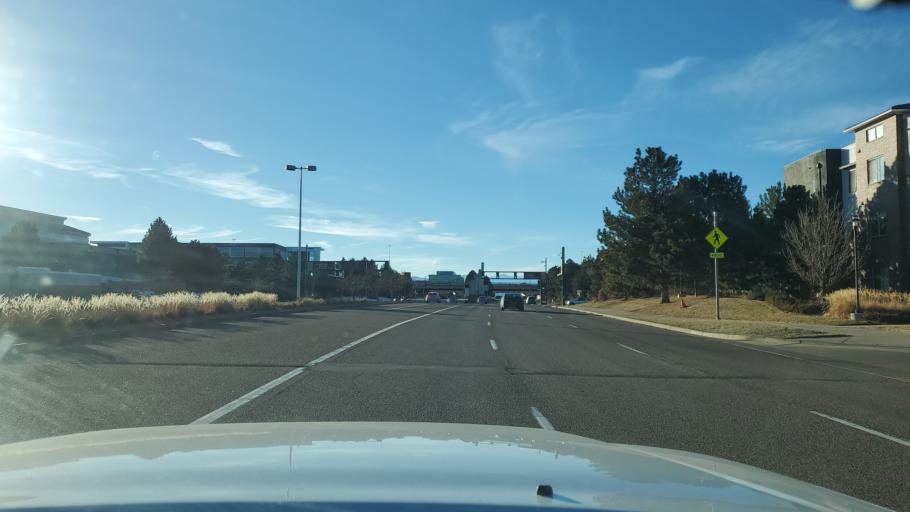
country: US
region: Colorado
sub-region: Arapahoe County
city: Centennial
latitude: 39.5806
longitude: -104.8721
